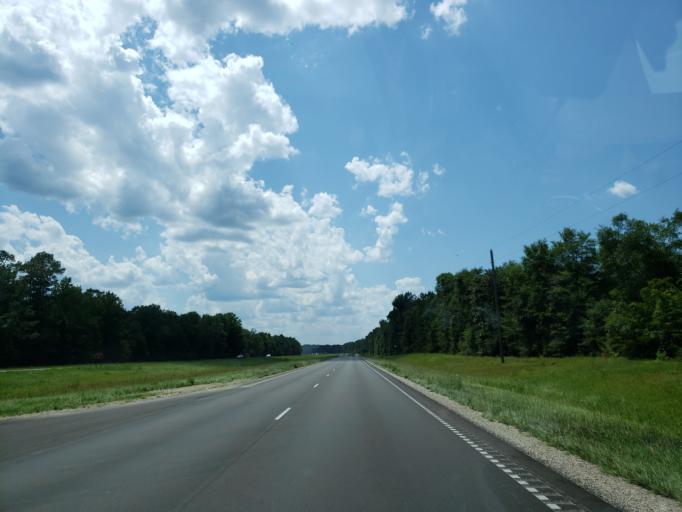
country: US
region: Mississippi
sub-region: Perry County
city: New Augusta
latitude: 31.2104
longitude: -89.1103
